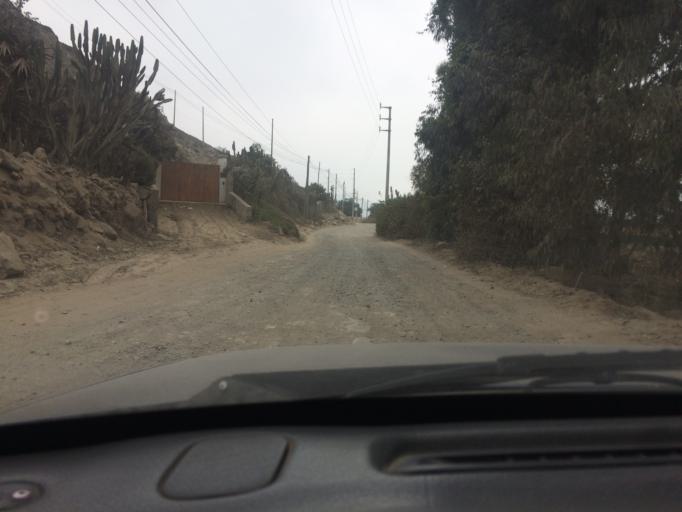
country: PE
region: Lima
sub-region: Lima
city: Cieneguilla
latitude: -12.1834
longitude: -76.8646
